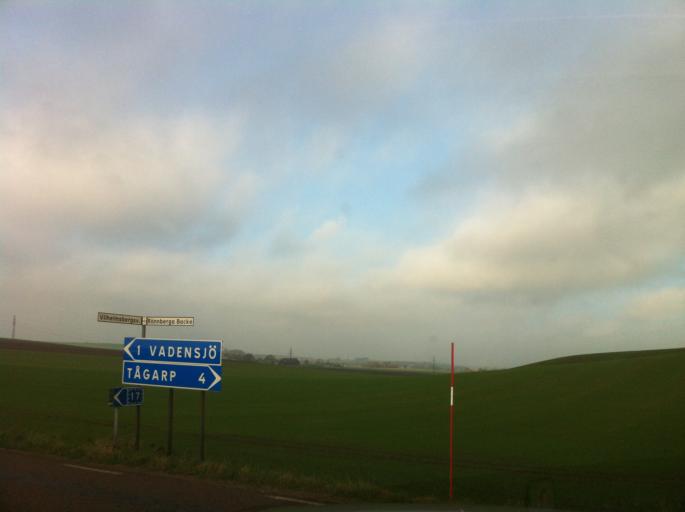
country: SE
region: Skane
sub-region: Landskrona
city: Asmundtorp
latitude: 55.9050
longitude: 12.9219
